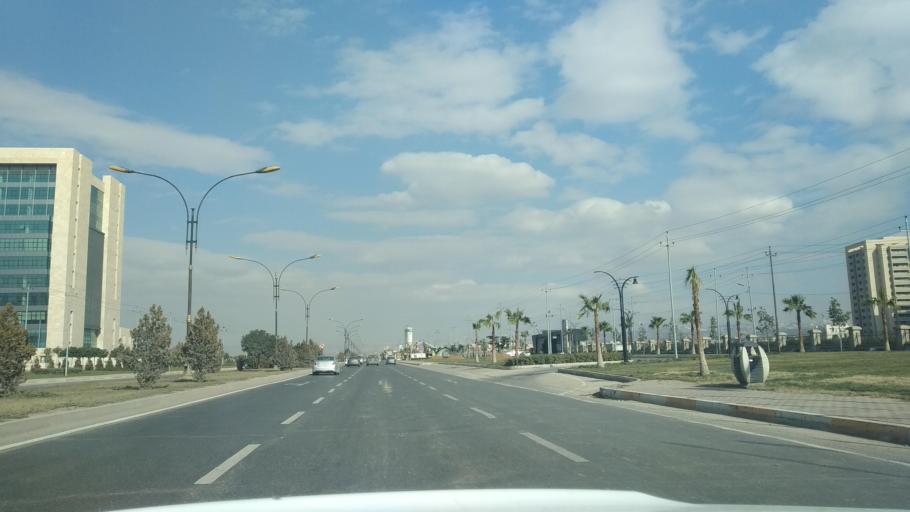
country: IQ
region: Arbil
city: Erbil
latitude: 36.2461
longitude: 44.0711
